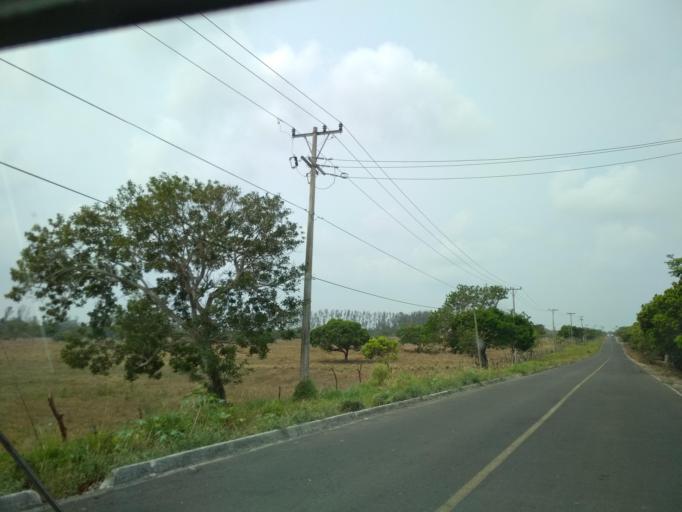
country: MX
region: Veracruz
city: Anton Lizardo
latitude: 19.0185
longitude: -95.9895
